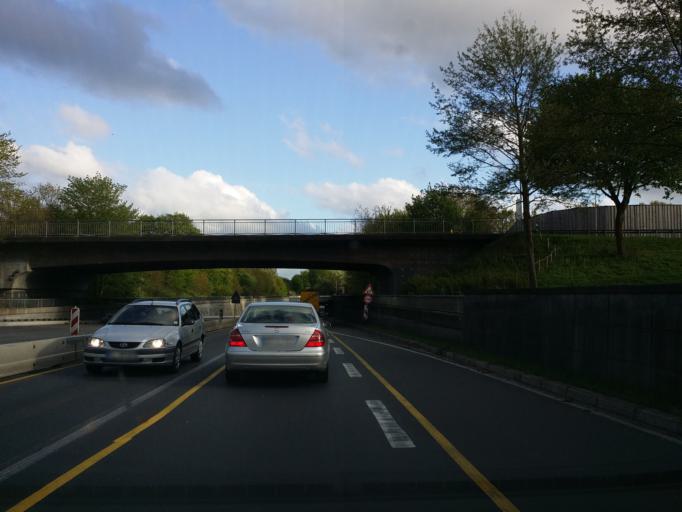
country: DE
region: Schleswig-Holstein
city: Westerronfeld
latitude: 54.2949
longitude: 9.6543
